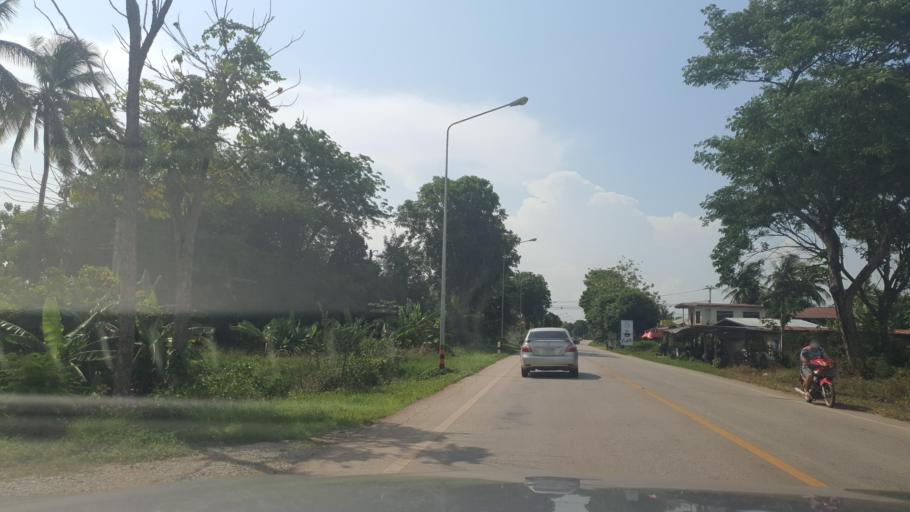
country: TH
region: Sukhothai
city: Si Samrong
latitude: 17.1938
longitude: 99.8503
